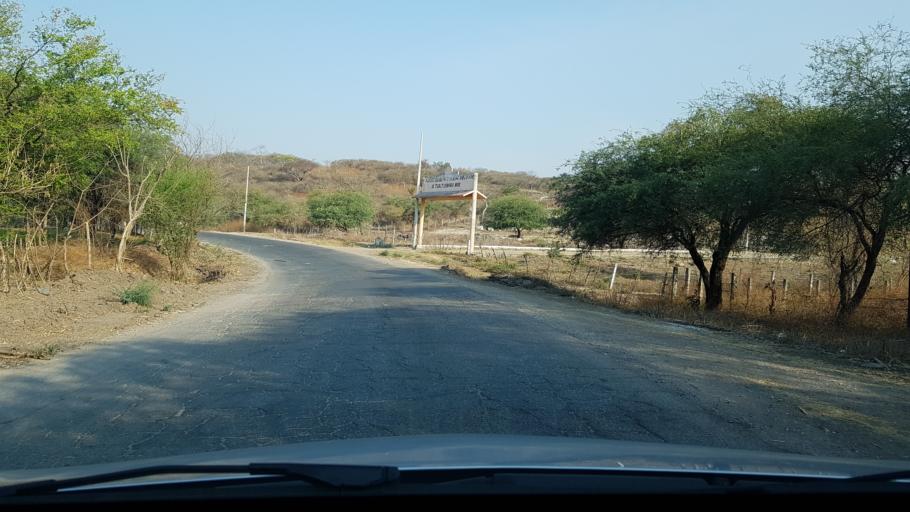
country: MX
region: Morelos
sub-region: Tlaltizapan de Zapata
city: Colonia Palo Prieto (Chipitongo)
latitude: 18.6912
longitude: -99.0959
